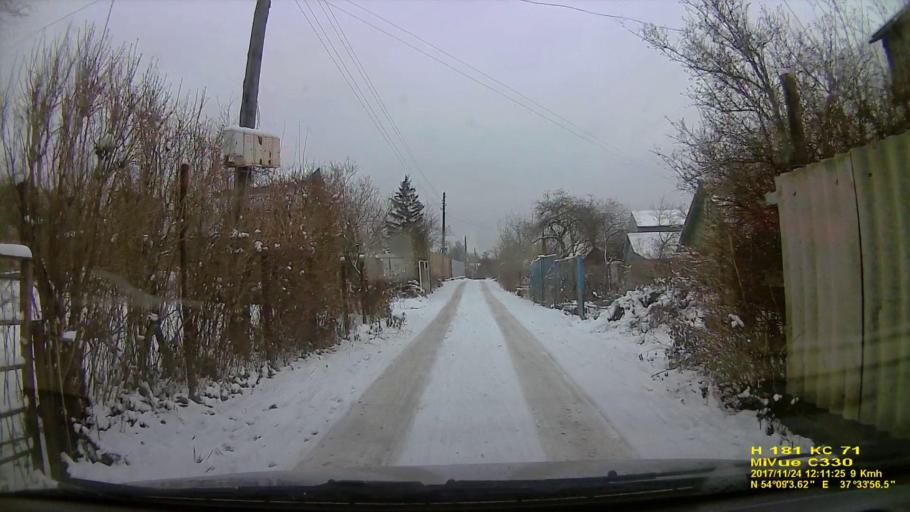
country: RU
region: Tula
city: Mendeleyevskiy
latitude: 54.1510
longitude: 37.5657
